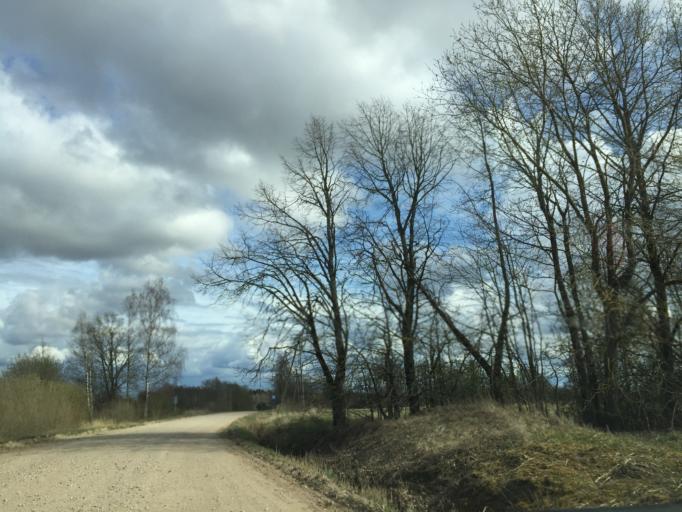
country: LV
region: Limbazu Rajons
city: Limbazi
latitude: 57.6142
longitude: 24.7228
